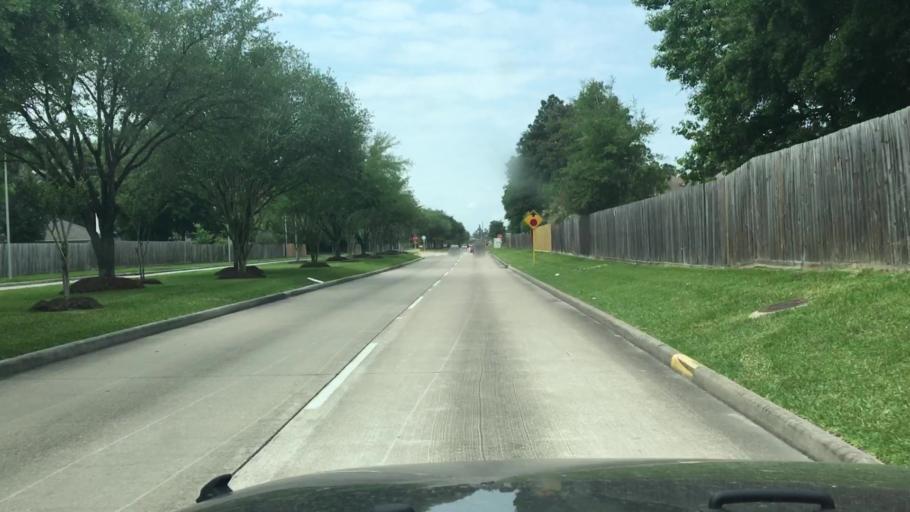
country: US
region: Texas
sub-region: Harris County
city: Atascocita
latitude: 29.9666
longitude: -95.2106
